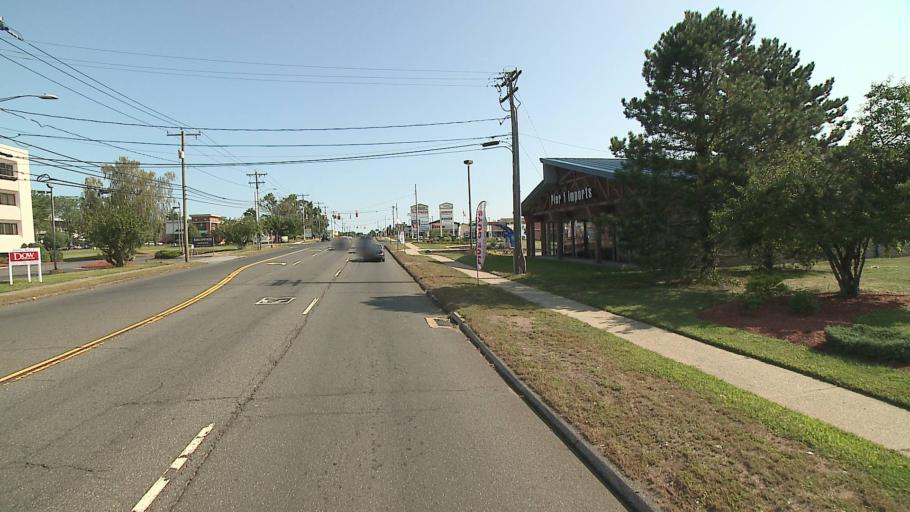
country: US
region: Connecticut
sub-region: New Haven County
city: Meriden
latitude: 41.5076
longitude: -72.8090
